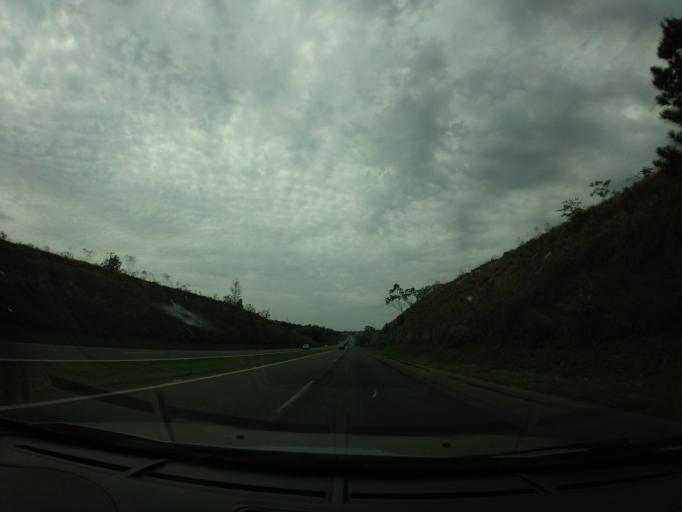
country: BR
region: Sao Paulo
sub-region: Piracicaba
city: Piracicaba
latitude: -22.7359
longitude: -47.5327
